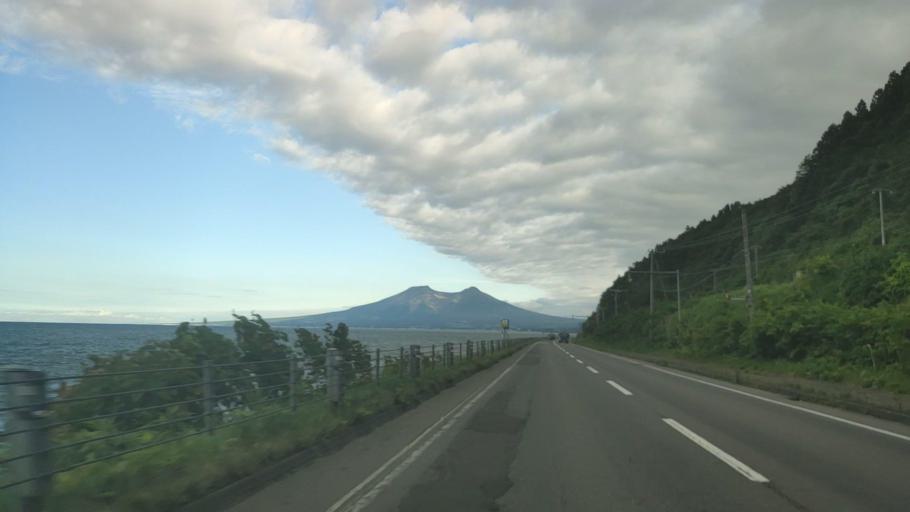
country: JP
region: Hokkaido
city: Nanae
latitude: 42.1497
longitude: 140.4942
